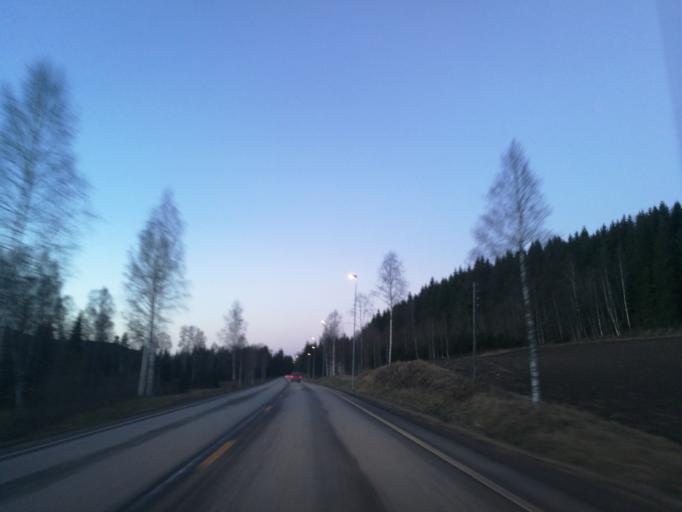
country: NO
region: Hedmark
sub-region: Kongsvinger
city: Kongsvinger
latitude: 60.1505
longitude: 12.0326
